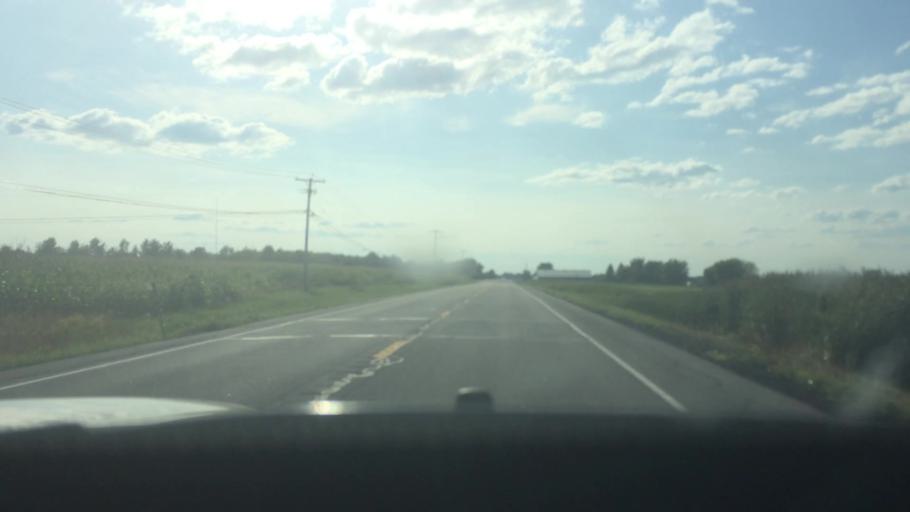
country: US
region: New York
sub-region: St. Lawrence County
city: Potsdam
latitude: 44.6890
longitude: -74.7183
